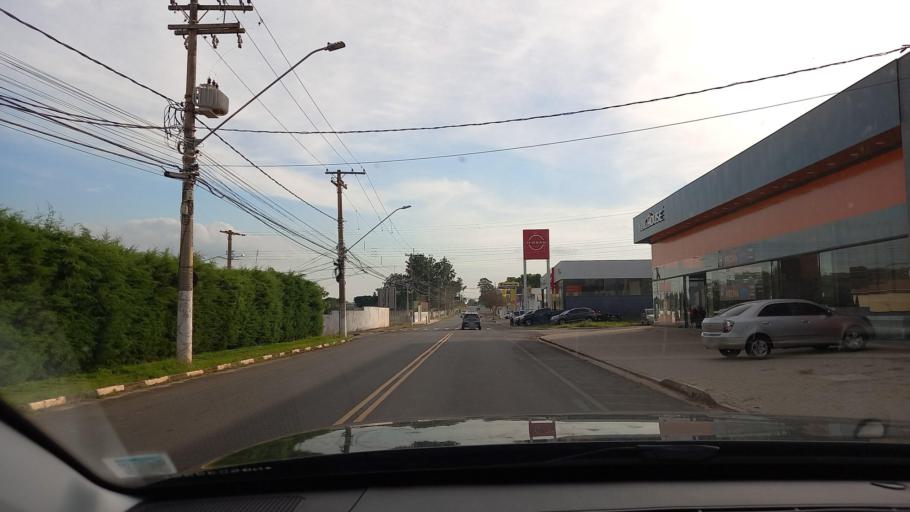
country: BR
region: Sao Paulo
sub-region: Mogi-Mirim
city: Mogi Mirim
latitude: -22.4450
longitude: -46.9744
